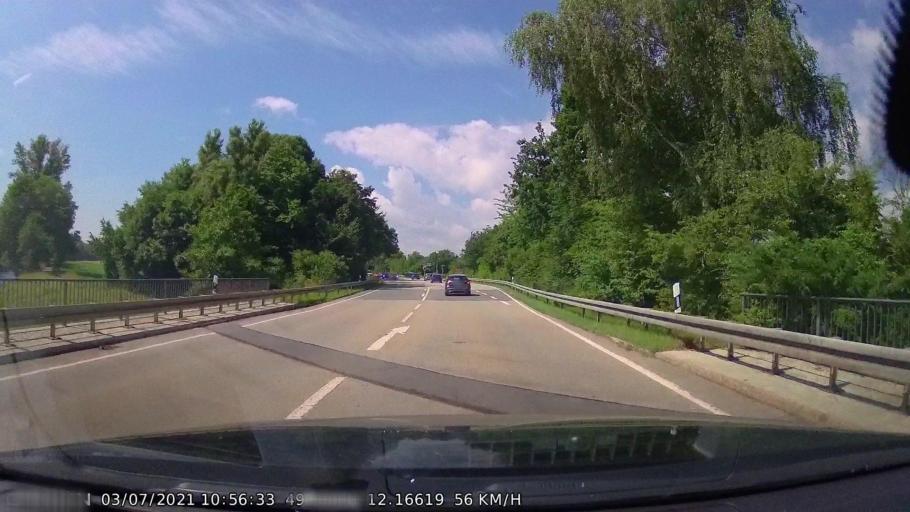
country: DE
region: Bavaria
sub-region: Upper Palatinate
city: Weiden
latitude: 49.6680
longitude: 12.1662
